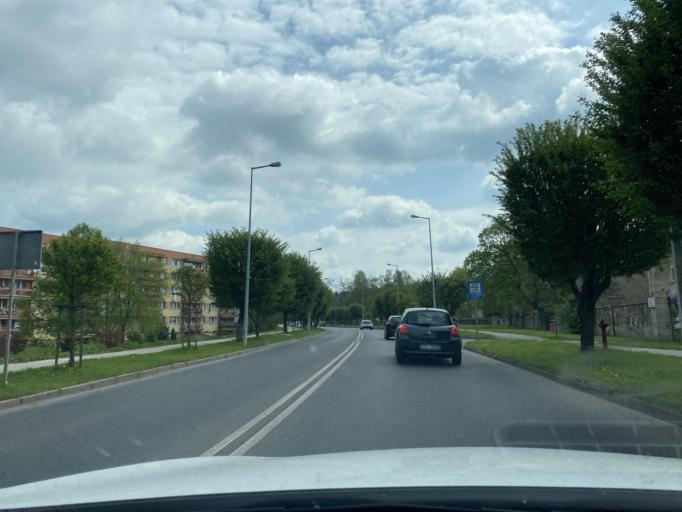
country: PL
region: Lower Silesian Voivodeship
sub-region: Powiat boleslawiecki
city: Boleslawiec
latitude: 51.2604
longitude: 15.5857
